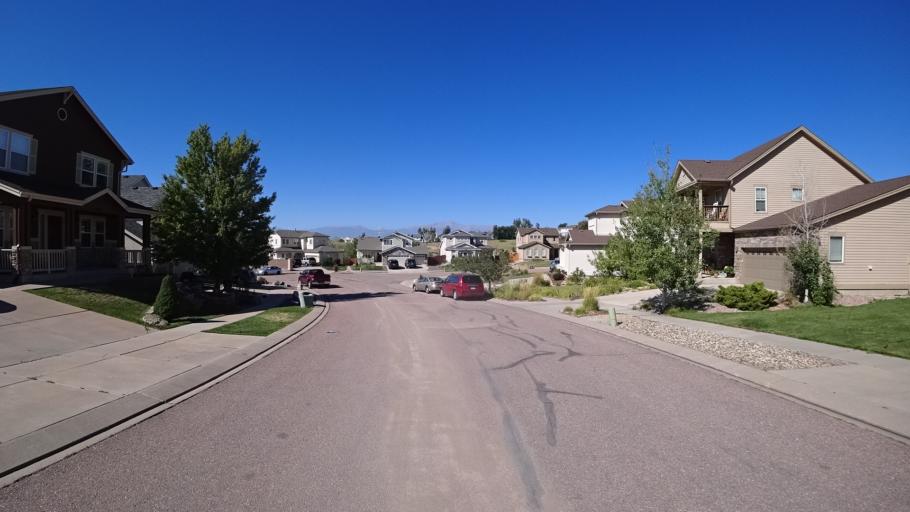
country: US
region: Colorado
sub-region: El Paso County
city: Black Forest
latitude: 38.9434
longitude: -104.7402
